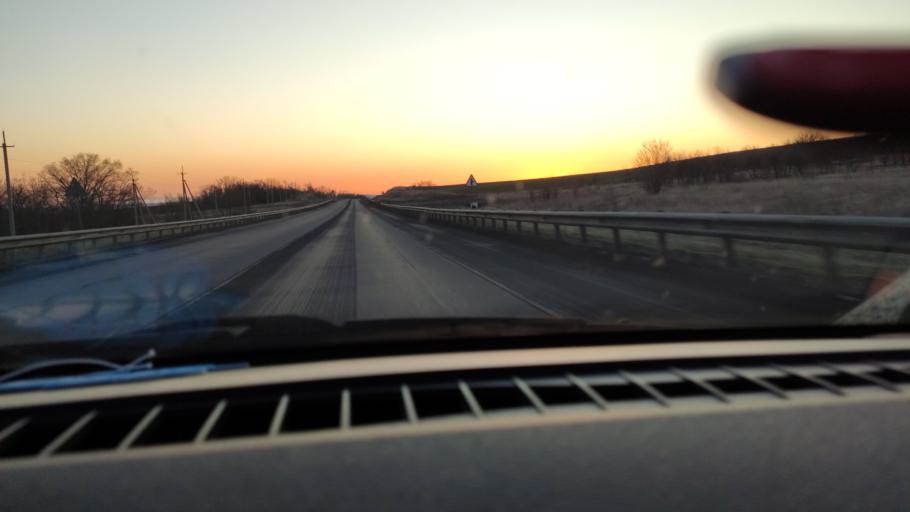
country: RU
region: Saratov
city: Shumeyka
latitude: 51.7825
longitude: 46.1290
